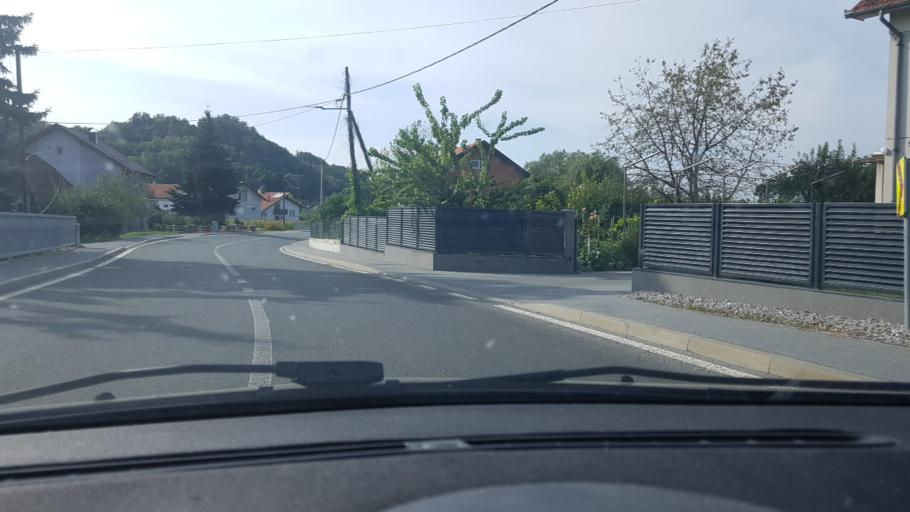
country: HR
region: Krapinsko-Zagorska
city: Zlatar
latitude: 46.0972
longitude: 16.0714
